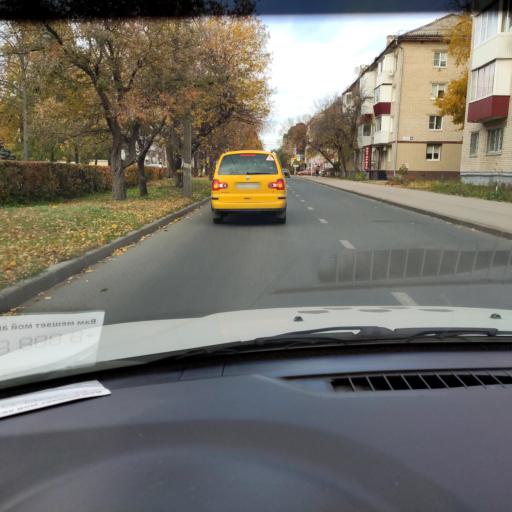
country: RU
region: Samara
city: Tol'yatti
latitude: 53.5066
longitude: 49.4126
